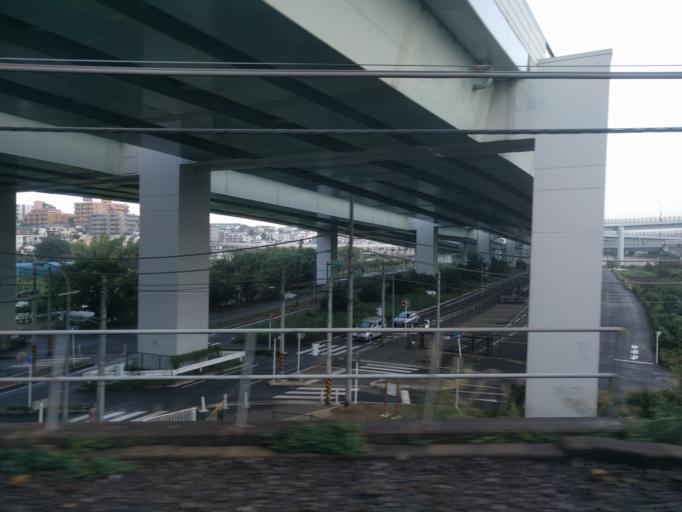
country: JP
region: Tokyo
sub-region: Machida-shi
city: Machida
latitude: 35.5472
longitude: 139.5373
